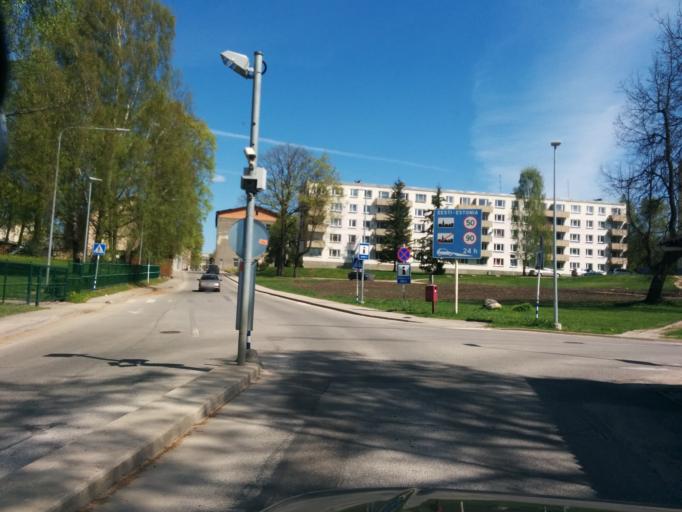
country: LV
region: Valkas Rajons
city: Valka
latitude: 57.7748
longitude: 26.0270
